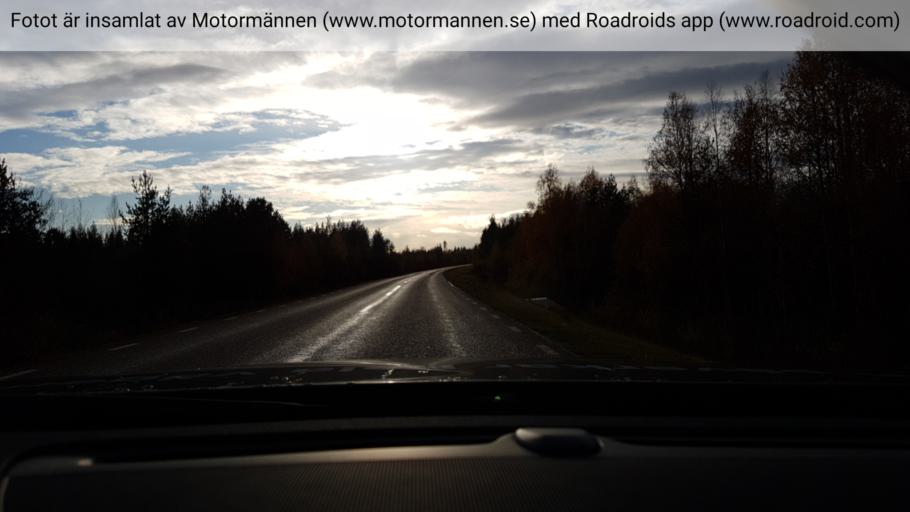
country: SE
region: Norrbotten
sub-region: Pajala Kommun
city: Pajala
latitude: 67.1700
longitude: 22.6751
